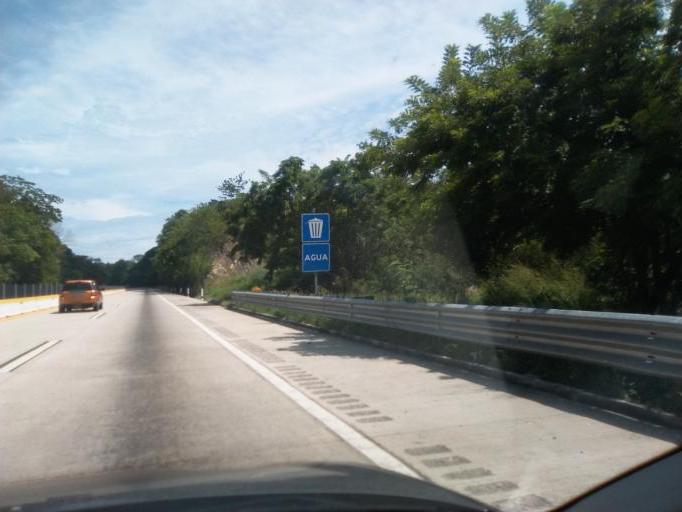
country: MX
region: Guerrero
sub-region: Acapulco de Juarez
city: Kilometro 30
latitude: 16.9509
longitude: -99.7581
